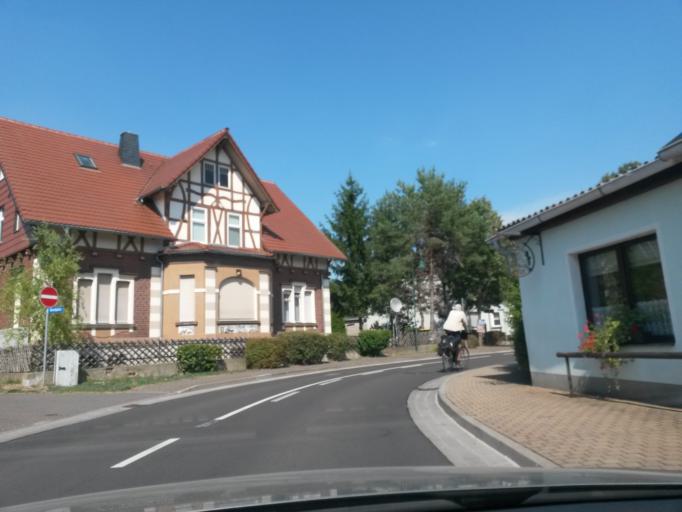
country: DE
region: Saxony-Anhalt
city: Jerichow
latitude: 52.4123
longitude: 11.9954
